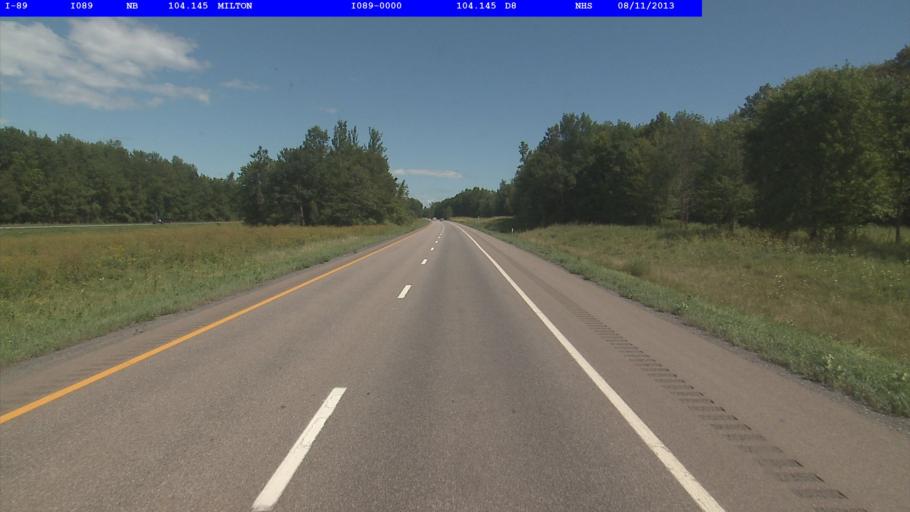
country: US
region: Vermont
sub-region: Chittenden County
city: Milton
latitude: 44.6724
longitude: -73.1320
